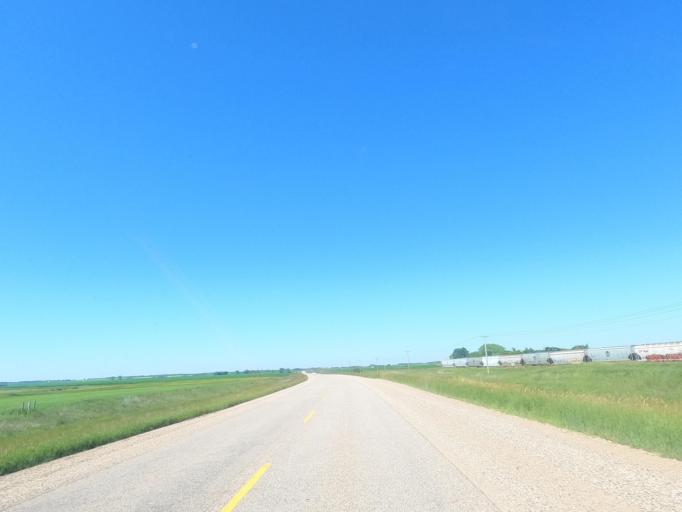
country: CA
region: Manitoba
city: Brandon
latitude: 49.5913
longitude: -99.9334
